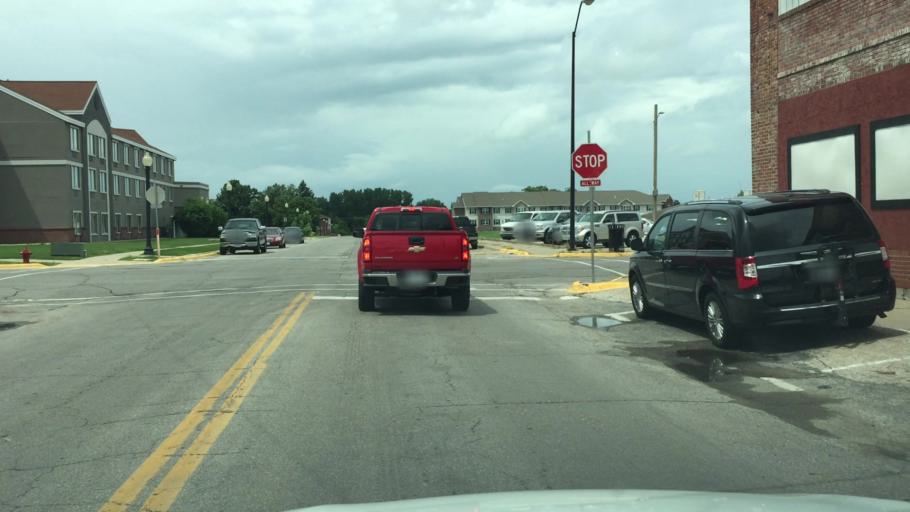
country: US
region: Iowa
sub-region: Jasper County
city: Newton
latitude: 41.7003
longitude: -93.0561
